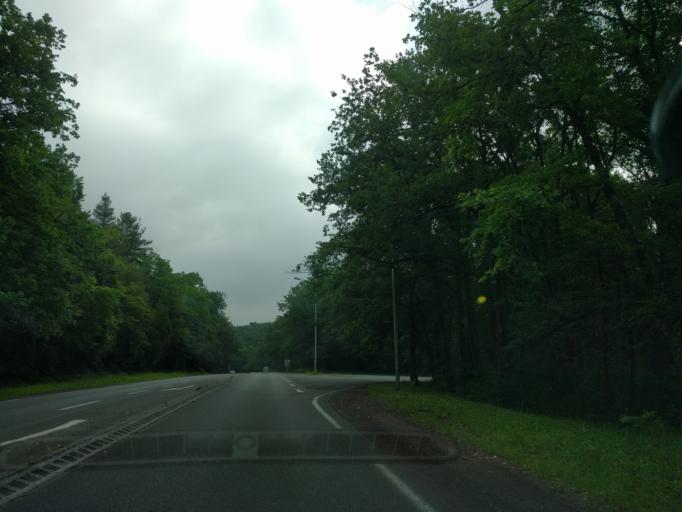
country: FR
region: Poitou-Charentes
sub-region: Departement de la Charente
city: Angouleme
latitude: 45.6348
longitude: 0.1443
